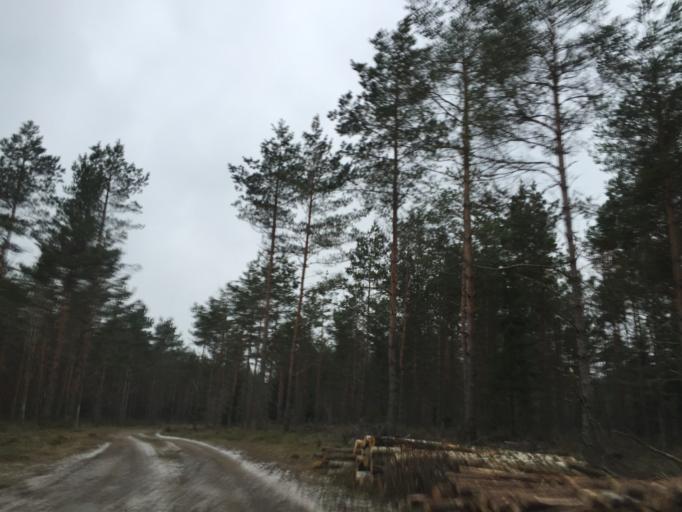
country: EE
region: Saare
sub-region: Kuressaare linn
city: Kuressaare
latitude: 58.3894
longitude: 22.2603
